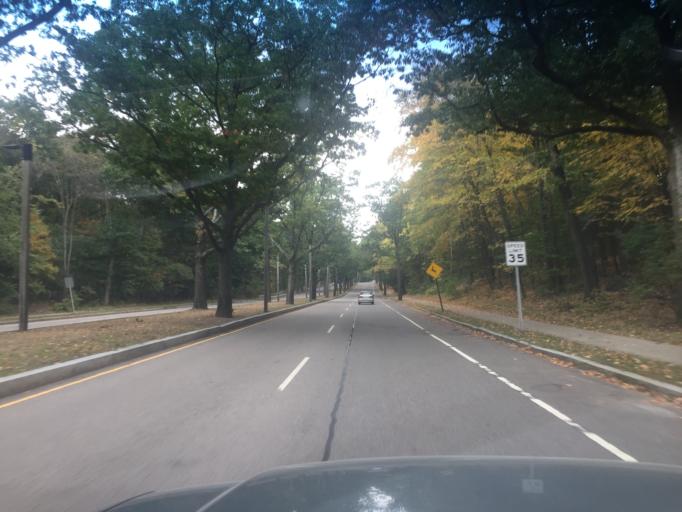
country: US
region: Massachusetts
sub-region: Suffolk County
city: Jamaica Plain
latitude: 42.2963
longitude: -71.1444
